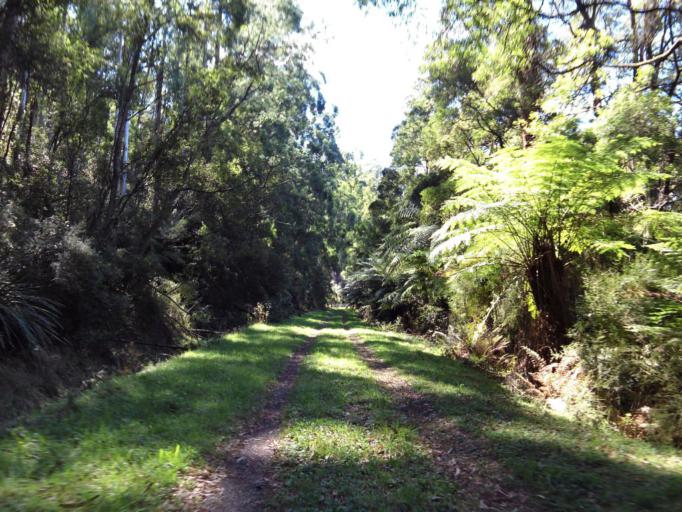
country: AU
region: Victoria
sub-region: Yarra Ranges
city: Millgrove
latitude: -37.7397
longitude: 145.6355
